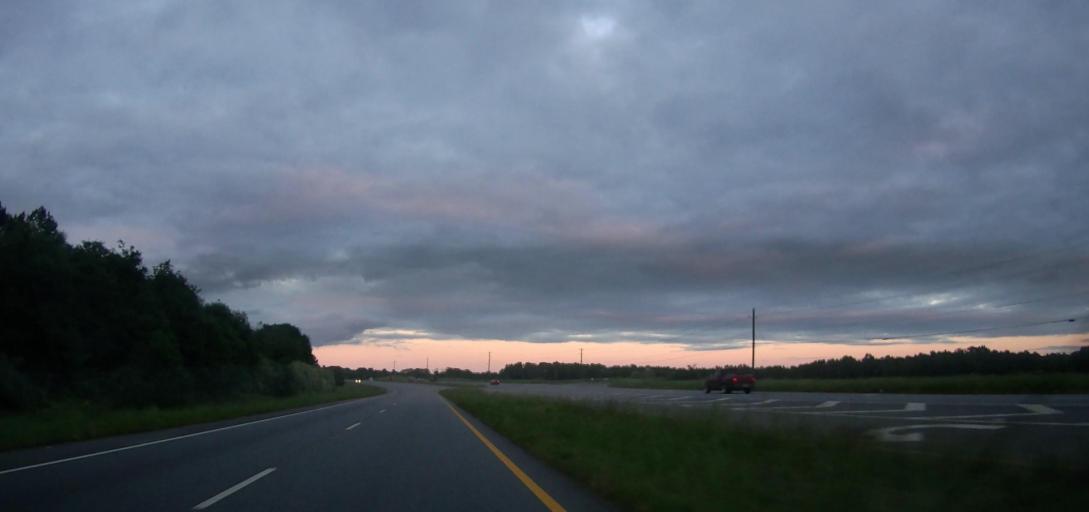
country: US
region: Georgia
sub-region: Jackson County
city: Arcade
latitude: 34.0623
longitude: -83.5260
